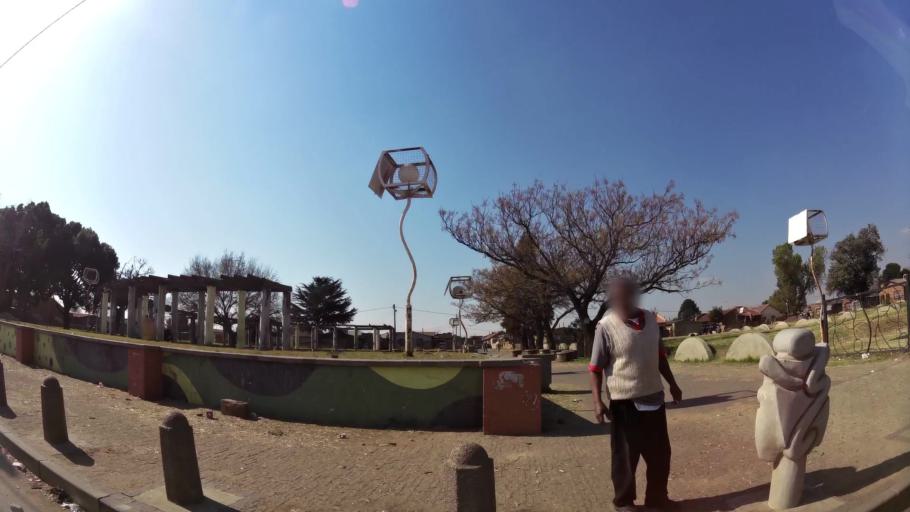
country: ZA
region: Gauteng
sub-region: Ekurhuleni Metropolitan Municipality
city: Boksburg
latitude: -26.2172
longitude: 28.2916
